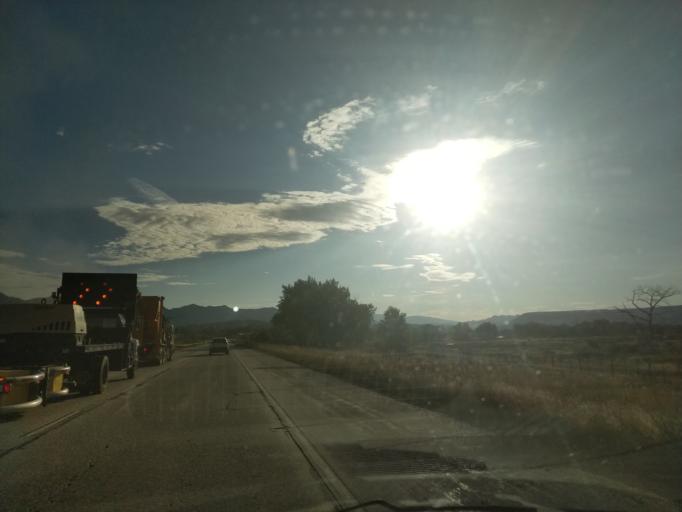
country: US
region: Colorado
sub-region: Garfield County
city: Silt
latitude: 39.5415
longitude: -107.6754
